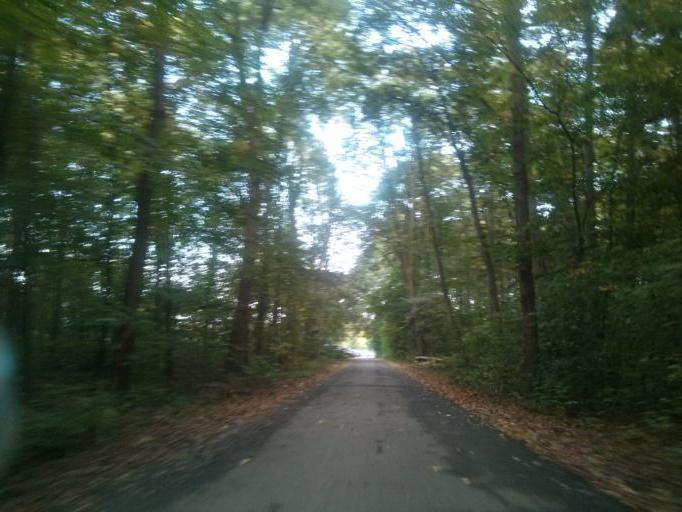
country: DE
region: North Rhine-Westphalia
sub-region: Regierungsbezirk Koln
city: Poll
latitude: 50.9045
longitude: 6.9975
